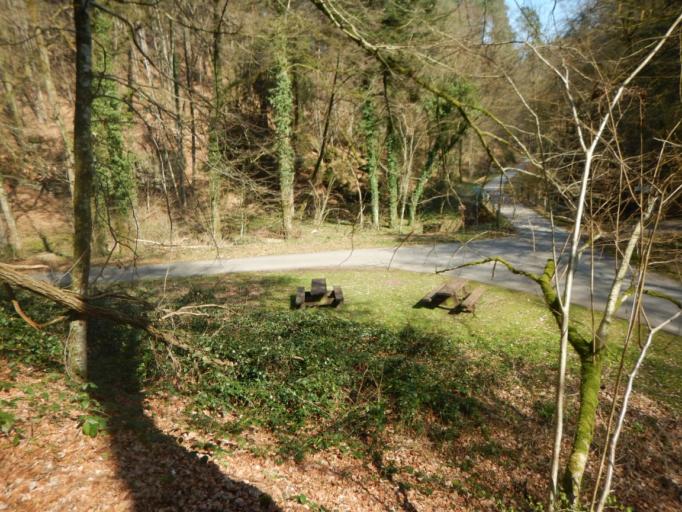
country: LU
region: Grevenmacher
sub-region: Canton d'Echternach
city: Berdorf
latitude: 49.7961
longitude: 6.3629
